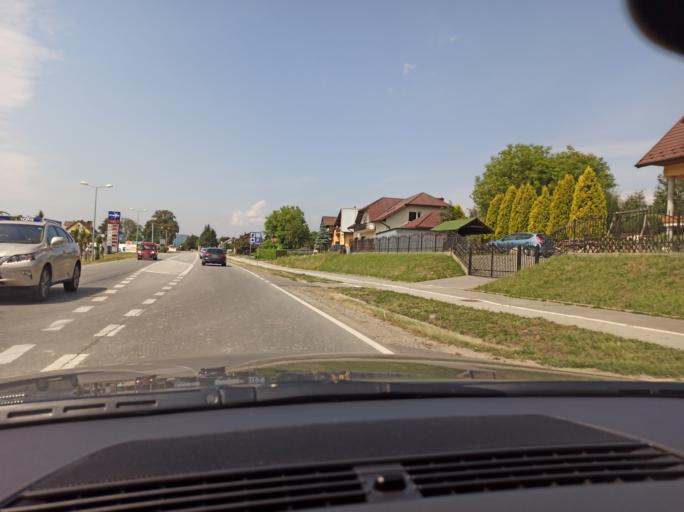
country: PL
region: Lesser Poland Voivodeship
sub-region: Powiat nowosadecki
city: Nowy Sacz
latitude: 49.6213
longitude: 20.7446
